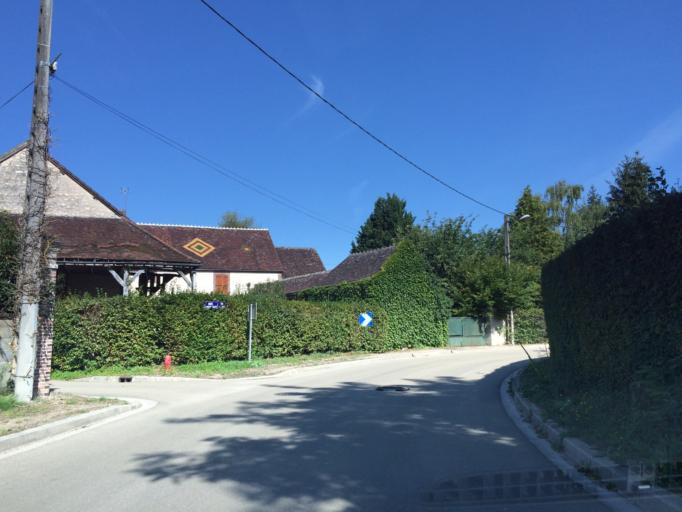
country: FR
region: Bourgogne
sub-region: Departement de l'Yonne
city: Aillant-sur-Tholon
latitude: 47.8323
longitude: 3.3612
